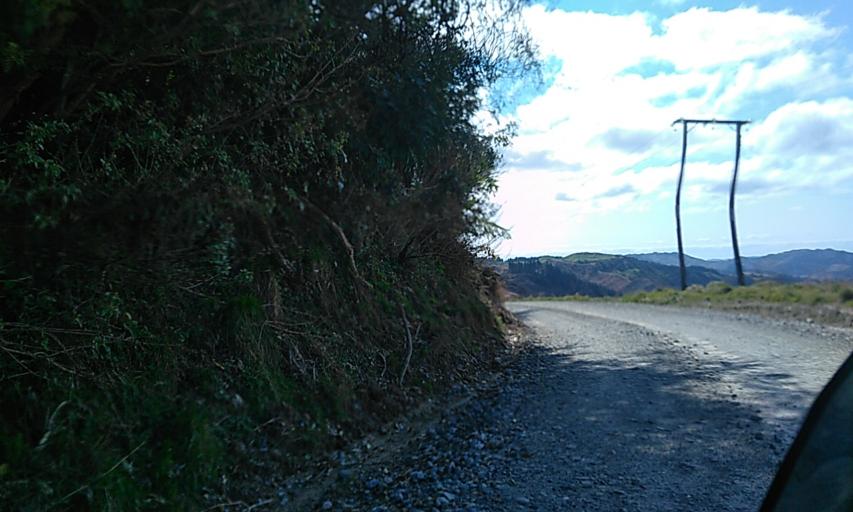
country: NZ
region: Gisborne
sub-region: Gisborne District
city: Gisborne
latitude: -38.2305
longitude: 178.0672
